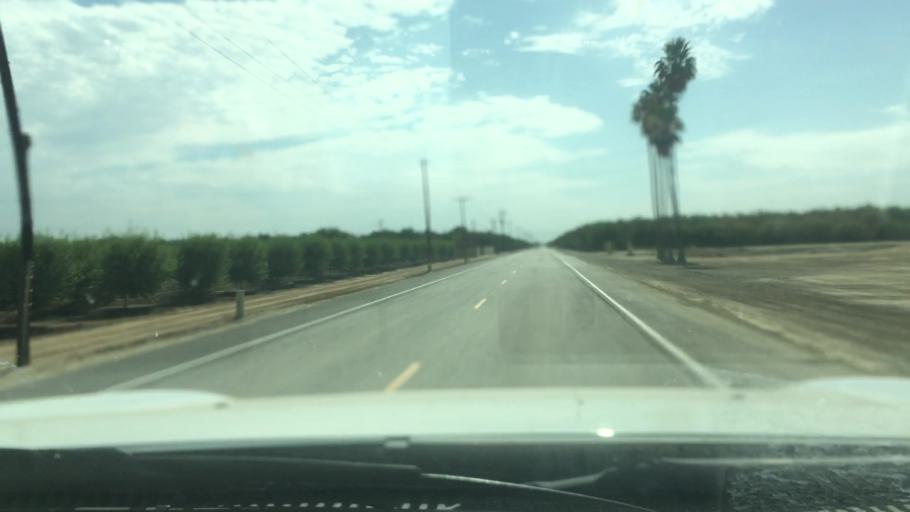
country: US
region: California
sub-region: Kern County
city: Wasco
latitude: 35.5577
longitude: -119.4496
